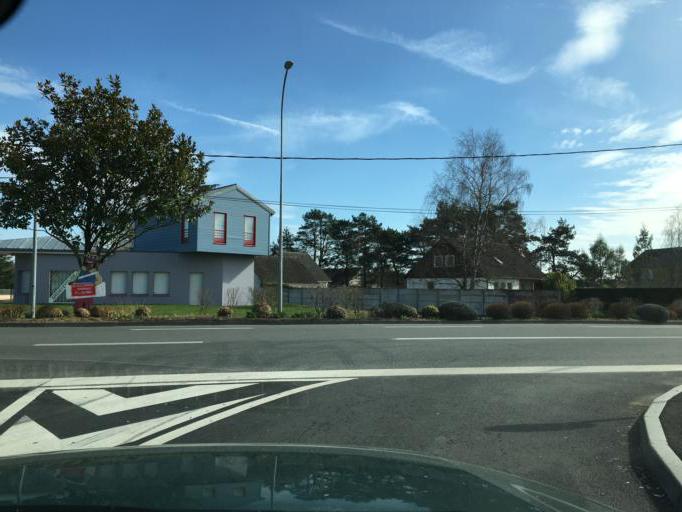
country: FR
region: Centre
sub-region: Departement du Loiret
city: Chateauneuf-sur-Loire
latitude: 47.8736
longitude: 2.2272
